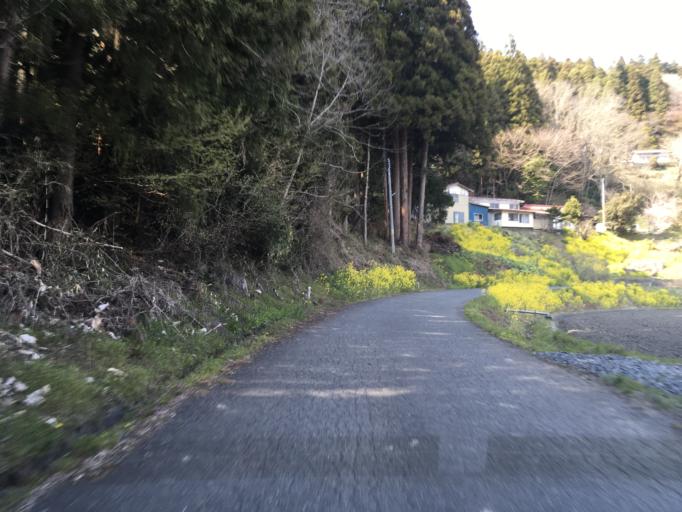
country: JP
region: Iwate
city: Ichinoseki
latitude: 38.8461
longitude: 141.3542
